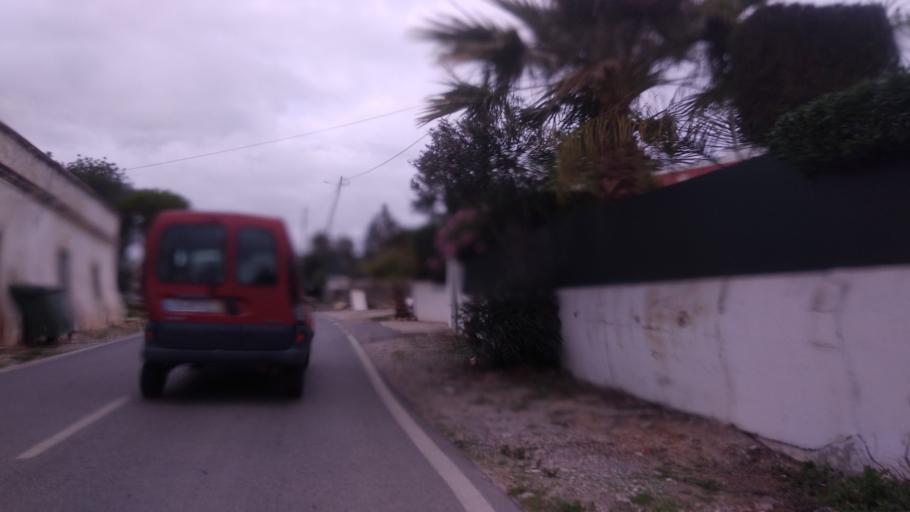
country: PT
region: Faro
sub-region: Faro
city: Santa Barbara de Nexe
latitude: 37.1092
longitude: -7.9623
